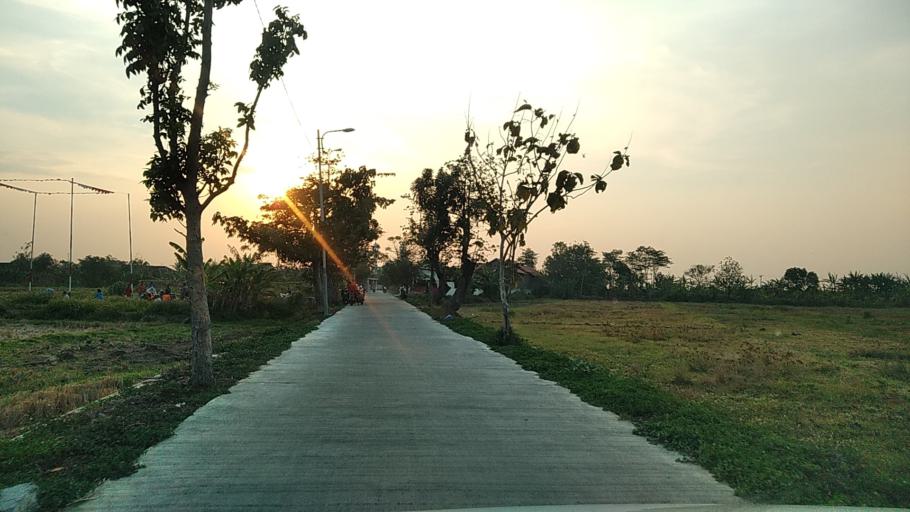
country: ID
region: Central Java
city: Semarang
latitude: -6.9589
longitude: 110.3058
